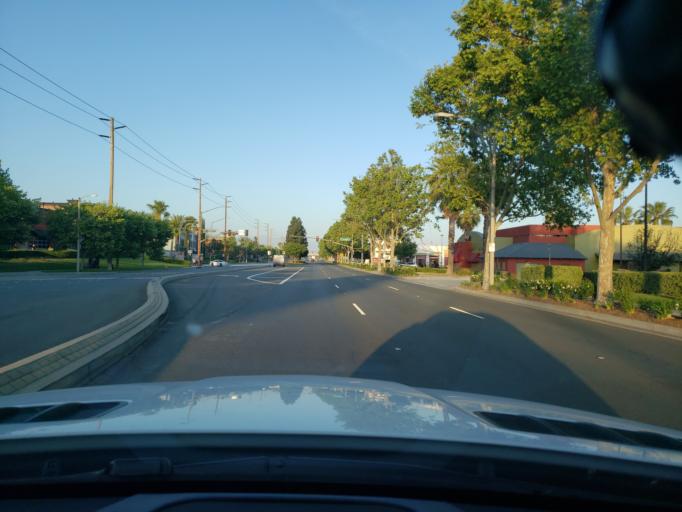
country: US
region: California
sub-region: San Bernardino County
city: Rancho Cucamonga
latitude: 34.0772
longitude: -117.5543
